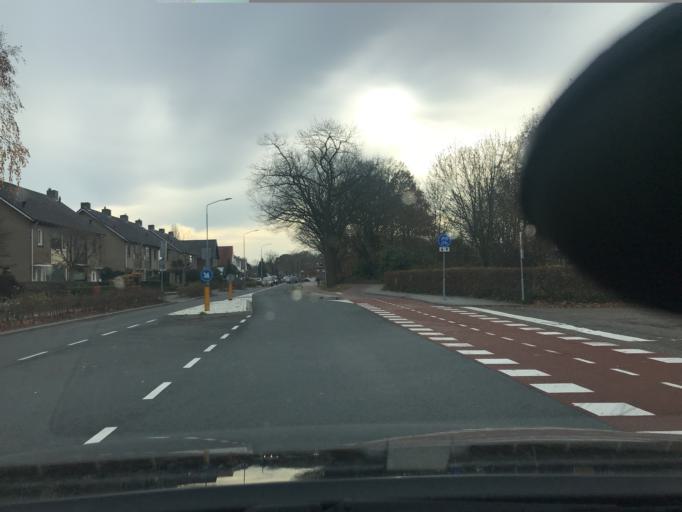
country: NL
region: Limburg
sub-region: Gemeente Venlo
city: Venlo
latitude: 51.3854
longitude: 6.1682
